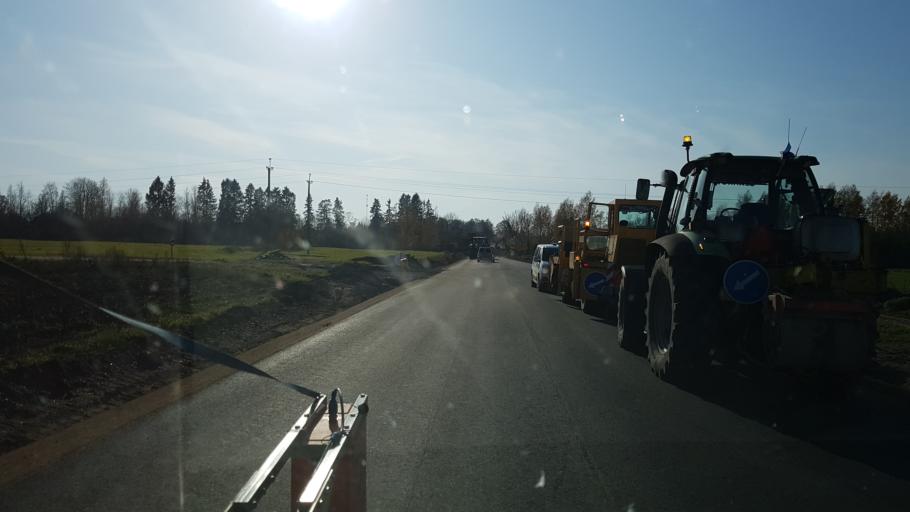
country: EE
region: Vorumaa
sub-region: Antsla vald
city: Vana-Antsla
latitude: 57.8359
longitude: 26.5430
